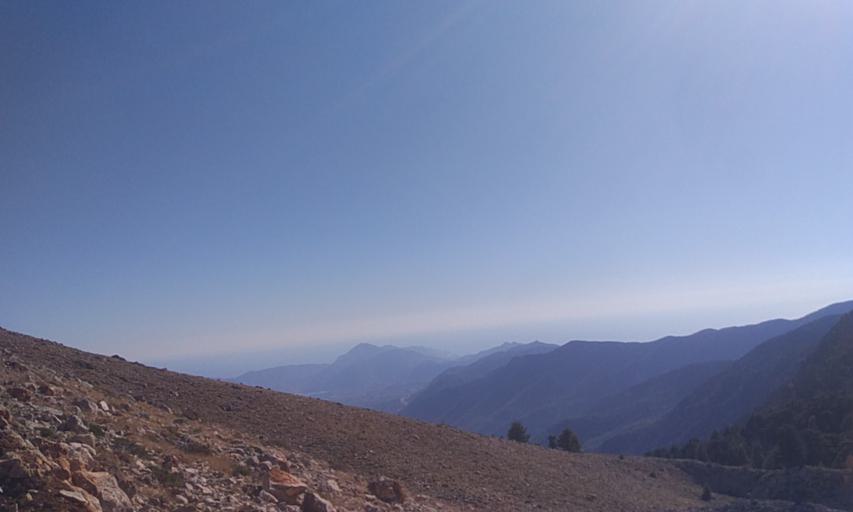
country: TR
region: Antalya
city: Altinyaka
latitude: 36.5406
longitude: 30.4210
